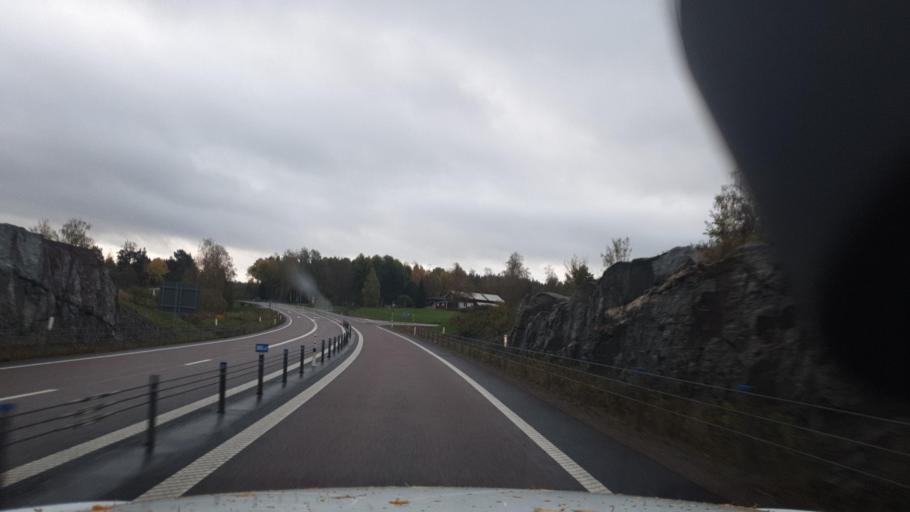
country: SE
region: Vaermland
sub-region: Eda Kommun
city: Amotfors
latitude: 59.7888
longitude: 12.3431
